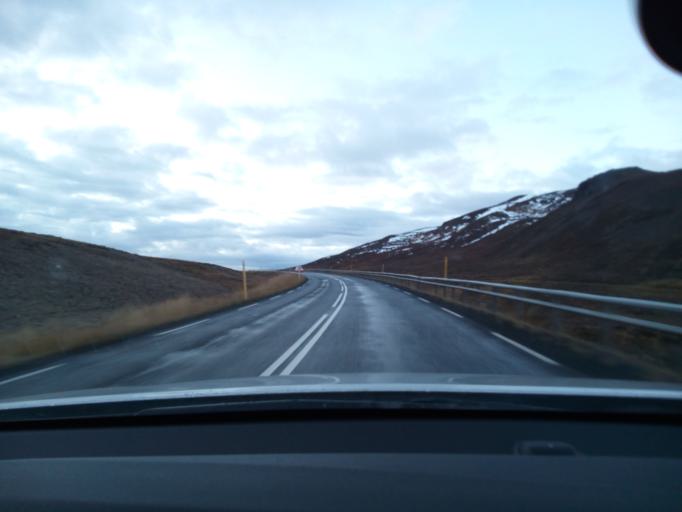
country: IS
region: Northeast
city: Akureyri
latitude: 65.8022
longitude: -17.9512
